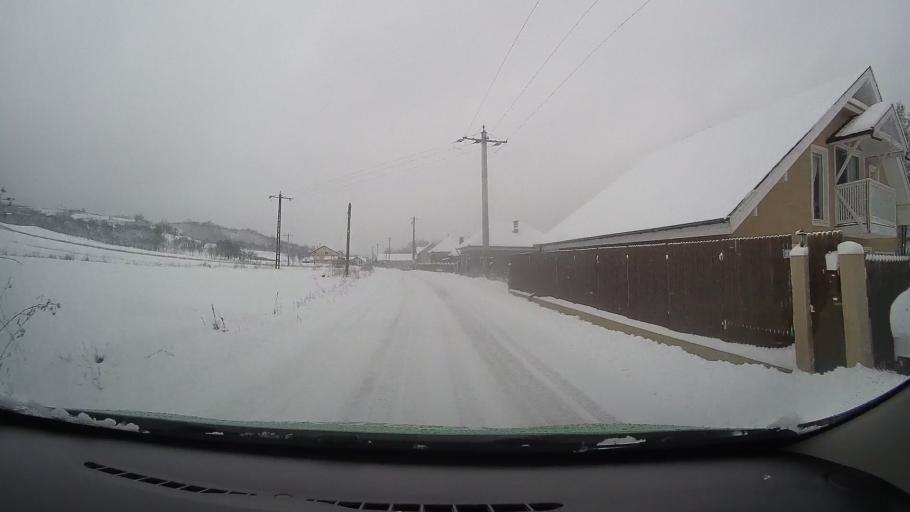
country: RO
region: Hunedoara
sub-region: Comuna Carjiti
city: Carjiti
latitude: 45.8306
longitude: 22.8433
